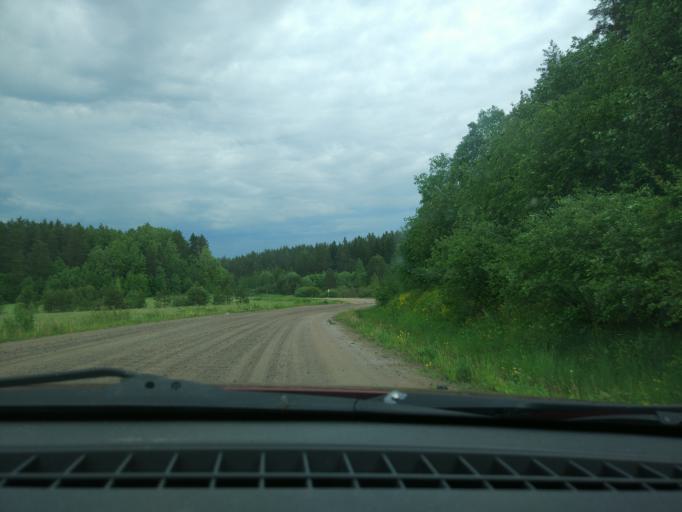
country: RU
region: Leningrad
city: Kuznechnoye
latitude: 61.2811
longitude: 29.8543
